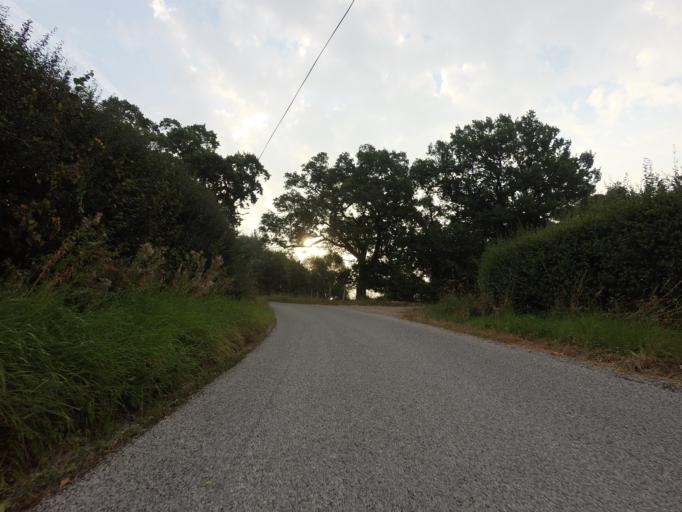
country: GB
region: England
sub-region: Kent
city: Lenham
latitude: 51.1595
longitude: 0.7637
